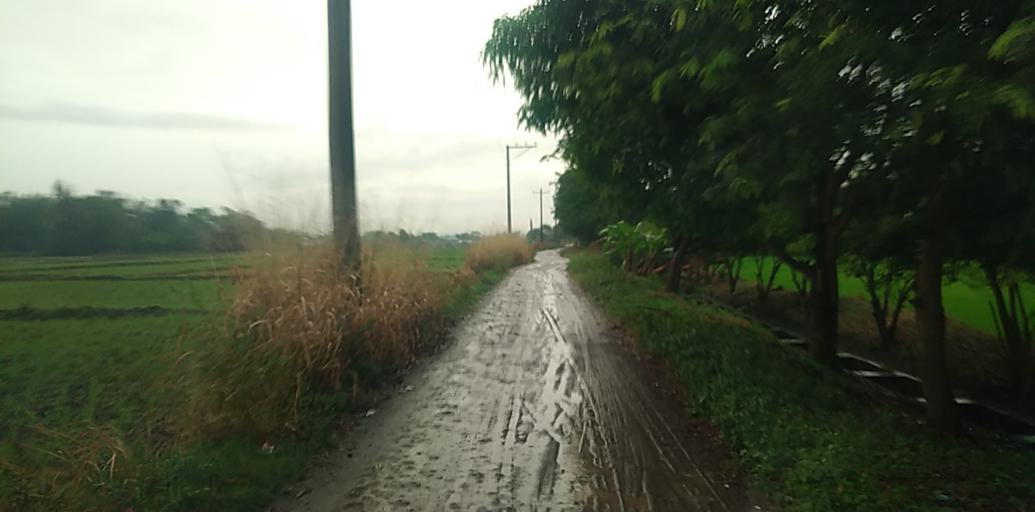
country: PH
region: Central Luzon
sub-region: Province of Pampanga
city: Panlinlang
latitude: 15.1592
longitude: 120.7174
